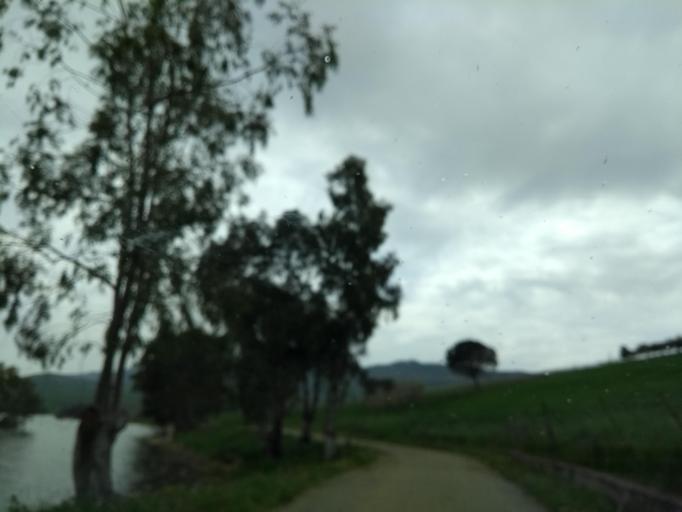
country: IT
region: Sicily
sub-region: Palermo
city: Partinico
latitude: 37.9925
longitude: 13.0823
